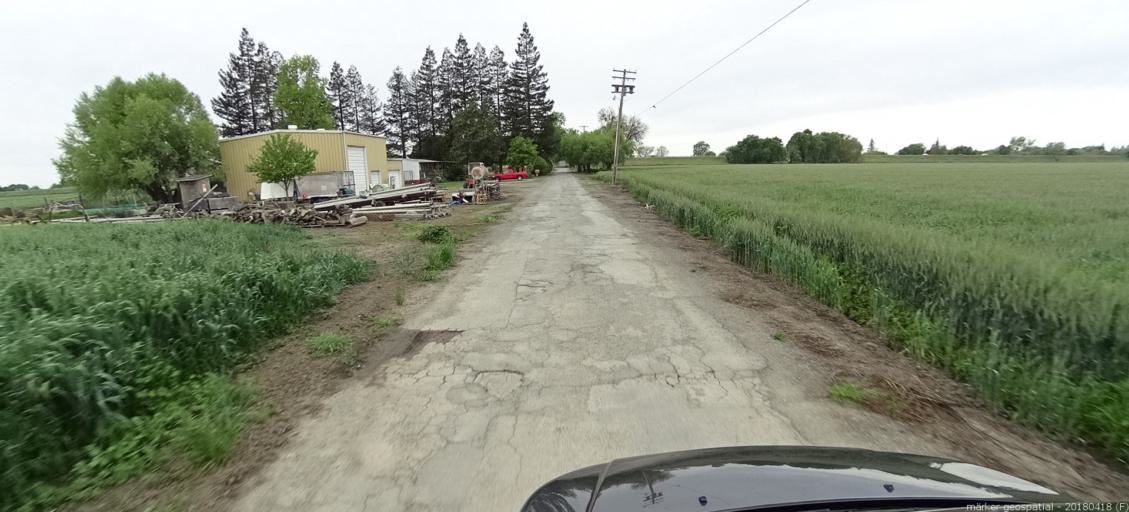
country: US
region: California
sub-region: Sacramento County
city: Laguna
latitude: 38.4113
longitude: -121.5124
